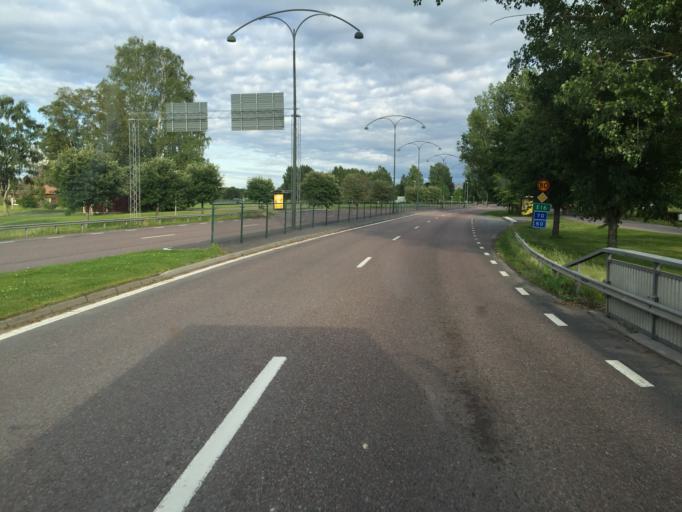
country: SE
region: Dalarna
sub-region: Borlange Kommun
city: Borlaenge
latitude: 60.4950
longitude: 15.4030
